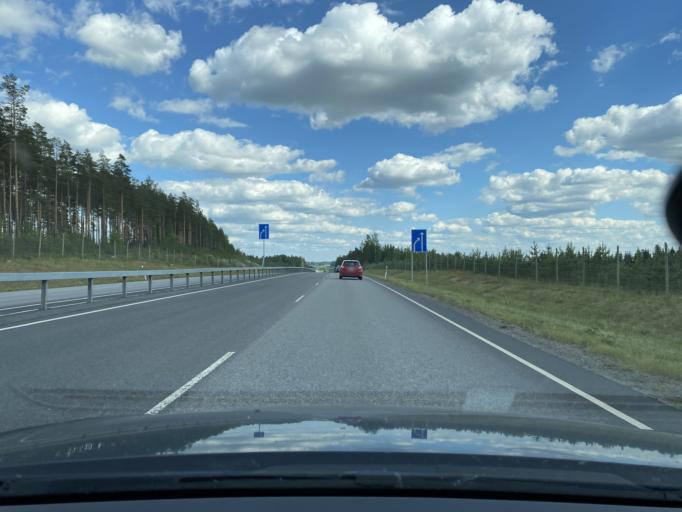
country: FI
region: Varsinais-Suomi
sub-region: Loimaa
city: Alastaro
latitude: 61.0515
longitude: 22.9600
